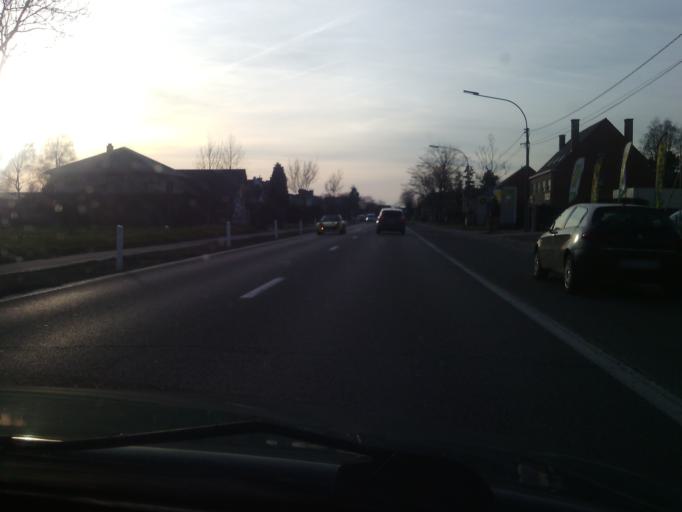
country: BE
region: Flanders
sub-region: Provincie Oost-Vlaanderen
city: Berlare
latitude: 51.0486
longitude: 3.9694
